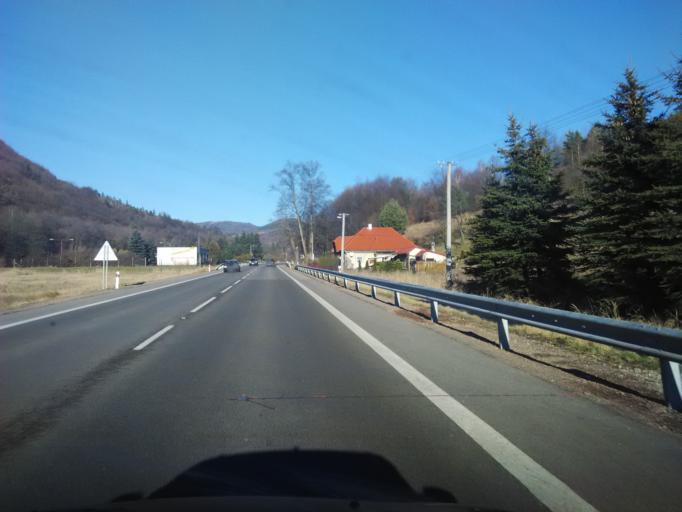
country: SK
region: Banskobystricky
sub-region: Okres Ziar nad Hronom
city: Kremnica
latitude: 48.6631
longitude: 18.9115
